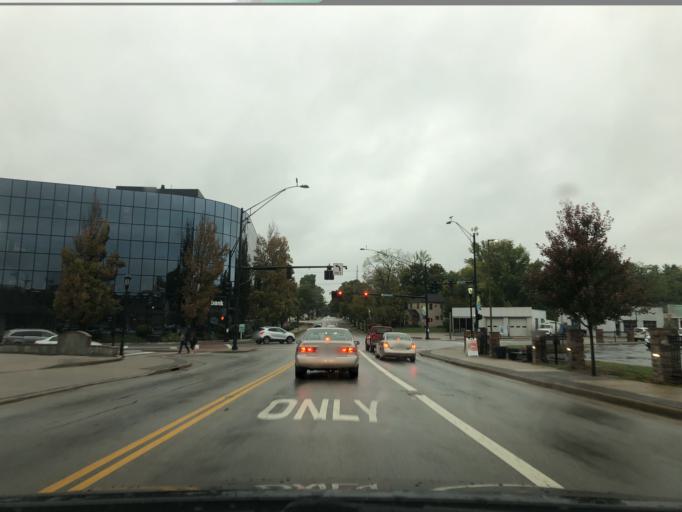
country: US
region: Ohio
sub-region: Hamilton County
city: Blue Ash
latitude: 39.2311
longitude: -84.3763
